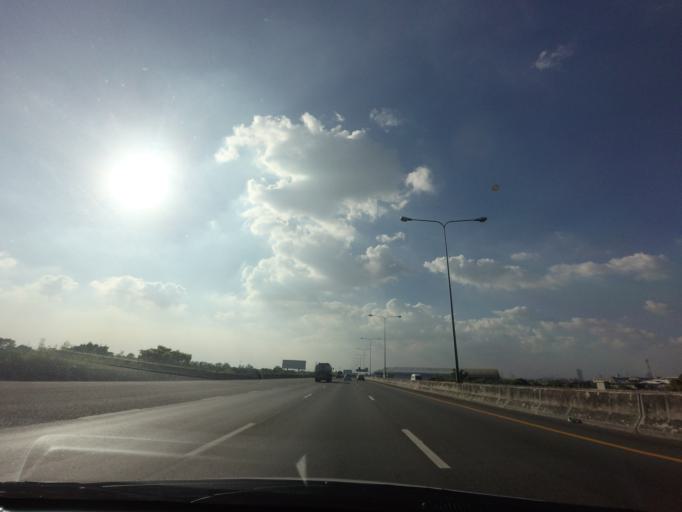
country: TH
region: Samut Prakan
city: Phra Samut Chedi
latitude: 13.6316
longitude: 100.5799
